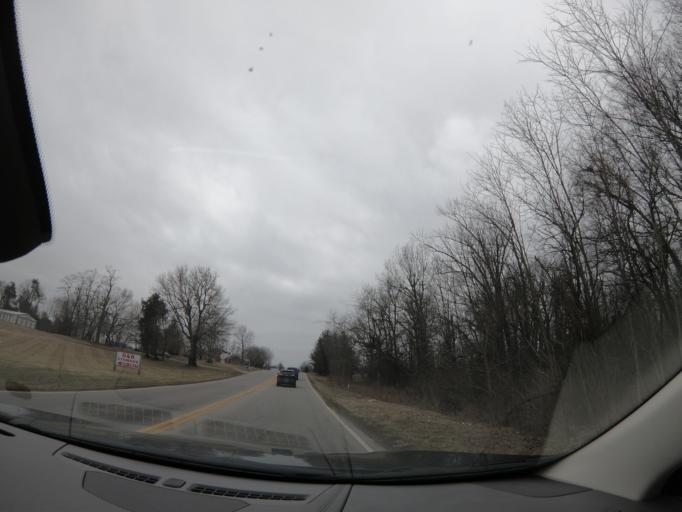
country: US
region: Kentucky
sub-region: Nelson County
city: Bardstown
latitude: 37.8482
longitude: -85.4596
